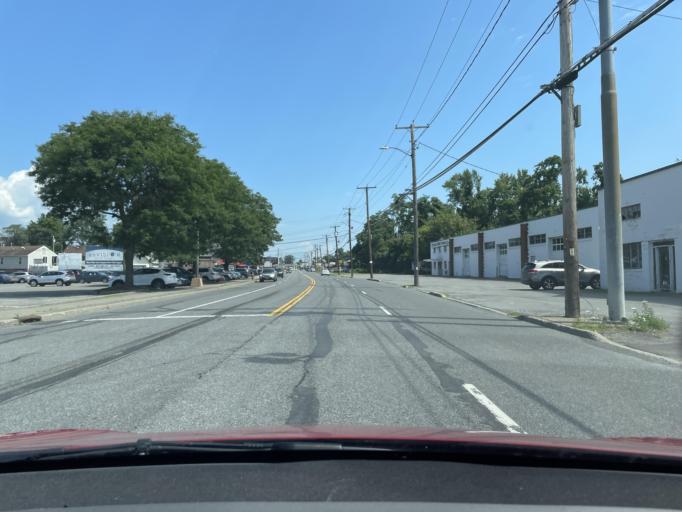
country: US
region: New York
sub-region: Ulster County
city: Lincoln Park
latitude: 41.9474
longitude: -73.9950
